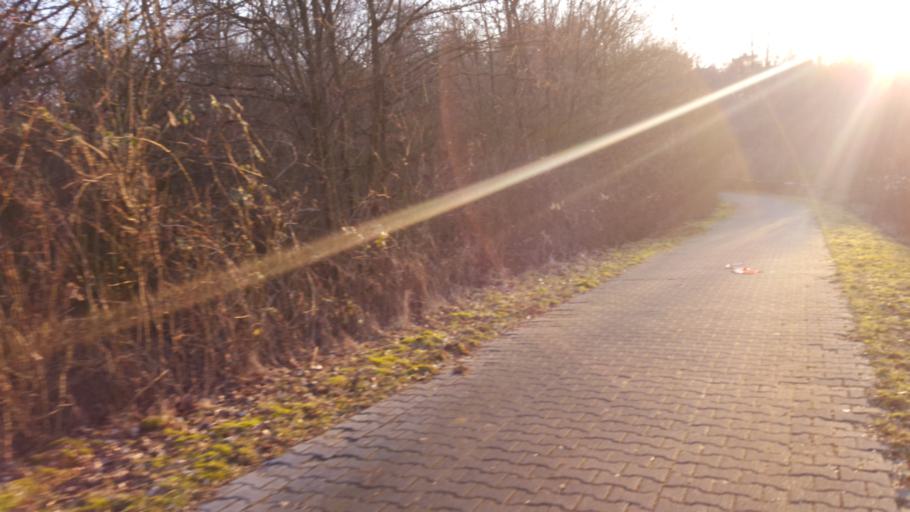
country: DE
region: North Rhine-Westphalia
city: Dorsten
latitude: 51.6617
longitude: 6.9920
